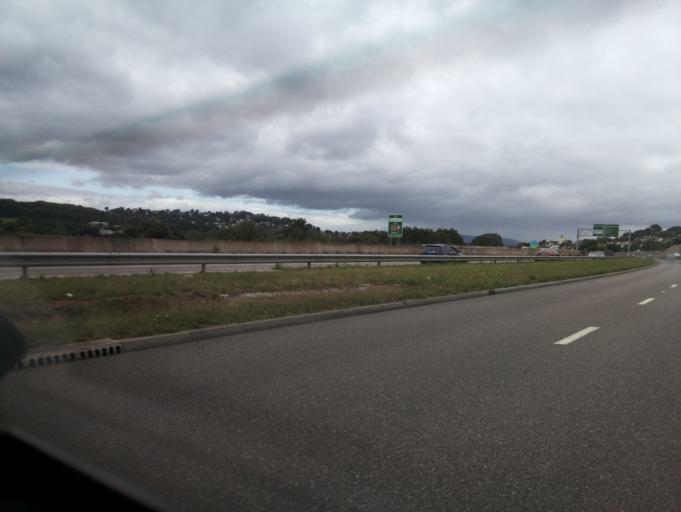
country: GB
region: England
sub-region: Devon
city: Kingskerswell
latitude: 50.5127
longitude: -3.5875
